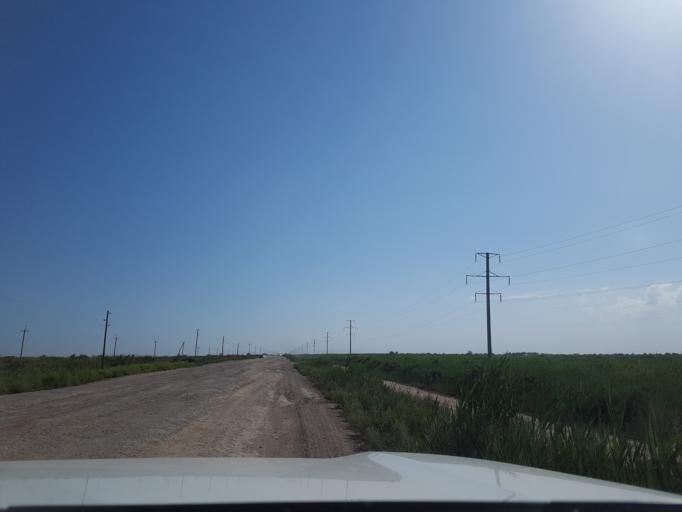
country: TM
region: Dasoguz
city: Koeneuergench
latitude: 42.1111
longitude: 58.9180
